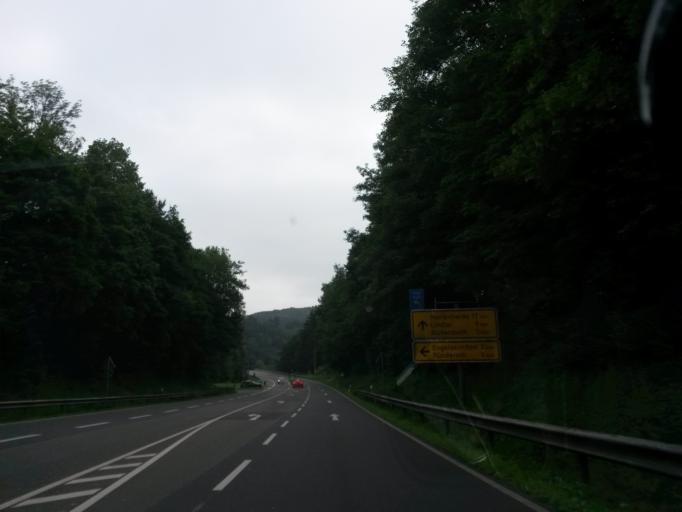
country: DE
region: North Rhine-Westphalia
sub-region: Regierungsbezirk Koln
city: Engelskirchen
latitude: 50.9843
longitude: 7.4317
